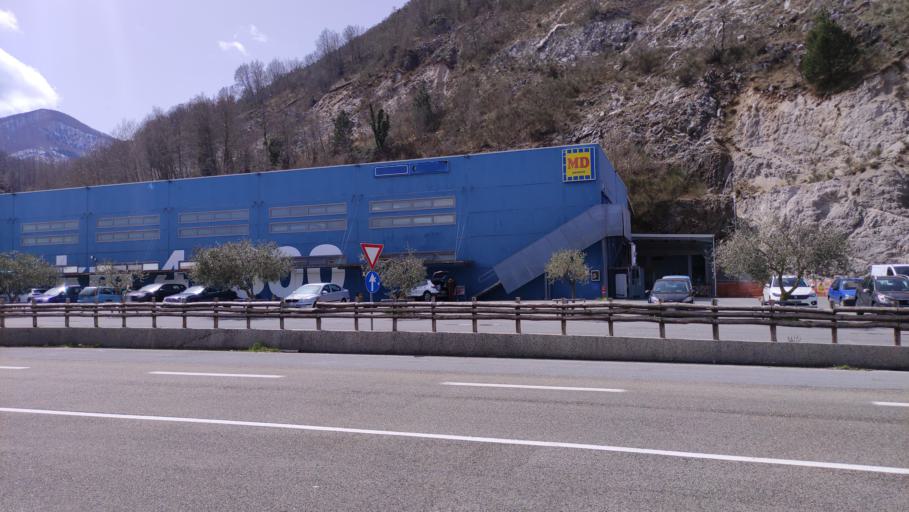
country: IT
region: Basilicate
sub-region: Provincia di Potenza
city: Lauria
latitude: 40.0786
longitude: 15.9085
